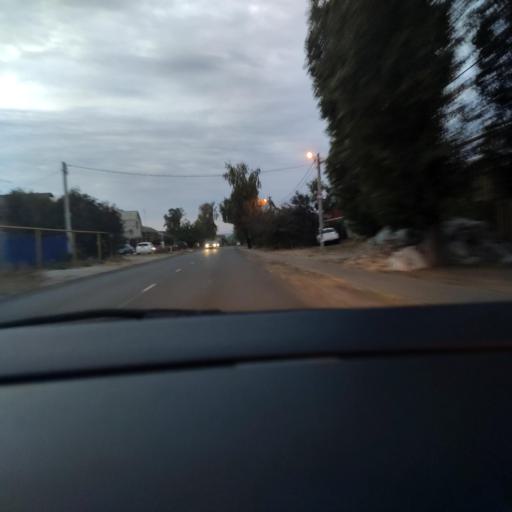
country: RU
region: Voronezj
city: Podgornoye
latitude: 51.7240
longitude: 39.1456
